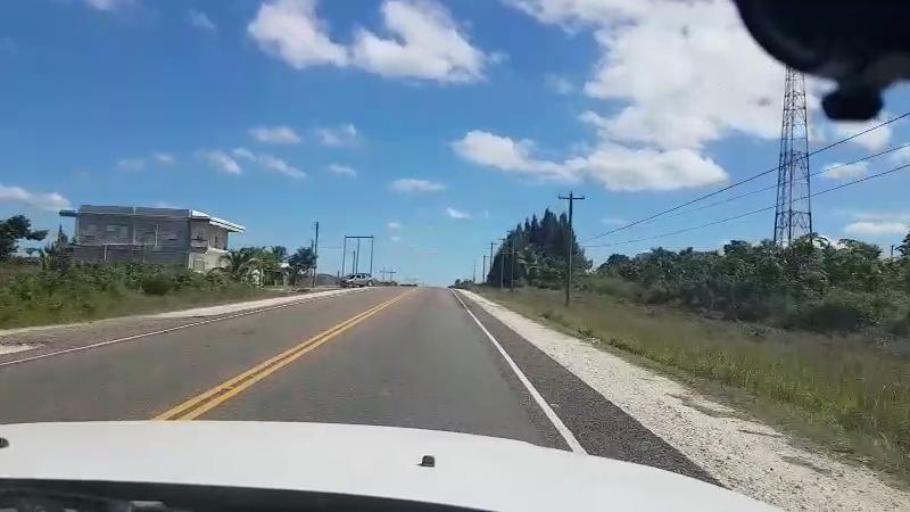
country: BZ
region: Cayo
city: Belmopan
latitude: 17.2770
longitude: -88.6615
